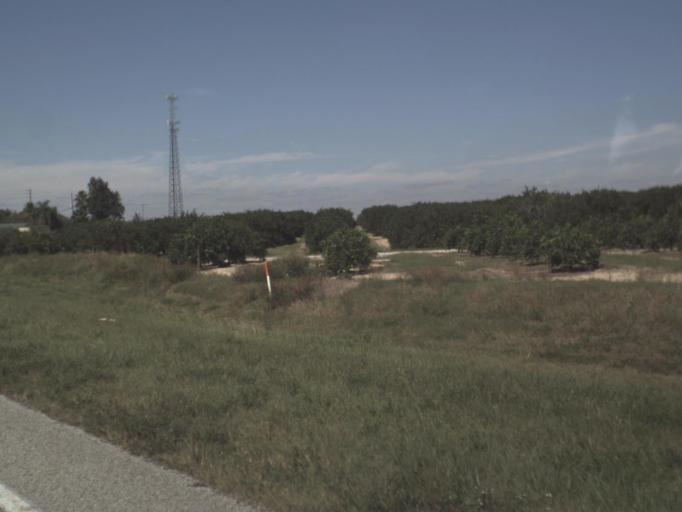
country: US
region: Florida
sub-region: Highlands County
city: Lake Placid
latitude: 27.3323
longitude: -81.3834
